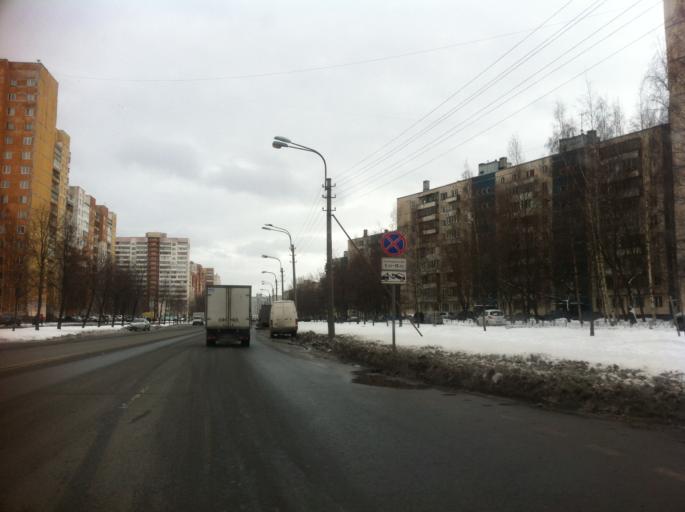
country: RU
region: St.-Petersburg
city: Uritsk
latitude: 59.8520
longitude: 30.2008
